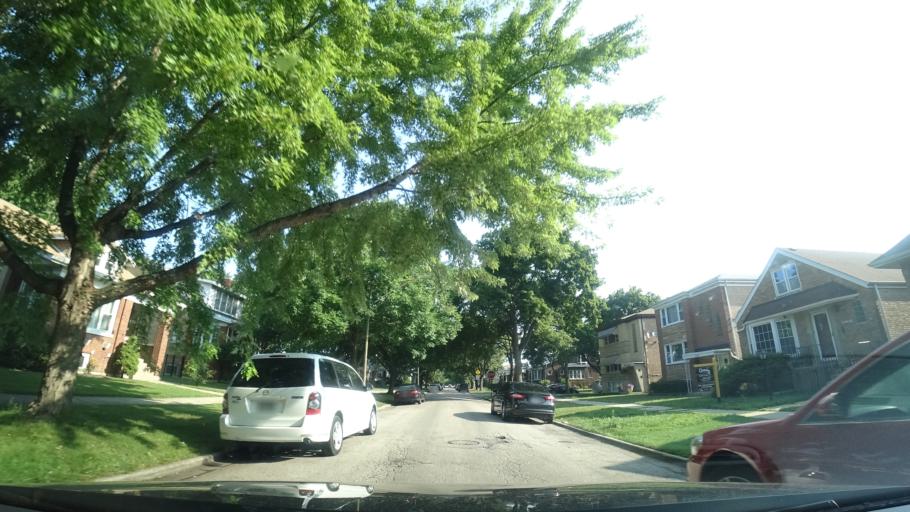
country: US
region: Illinois
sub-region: Cook County
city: Harwood Heights
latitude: 41.9733
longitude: -87.7734
